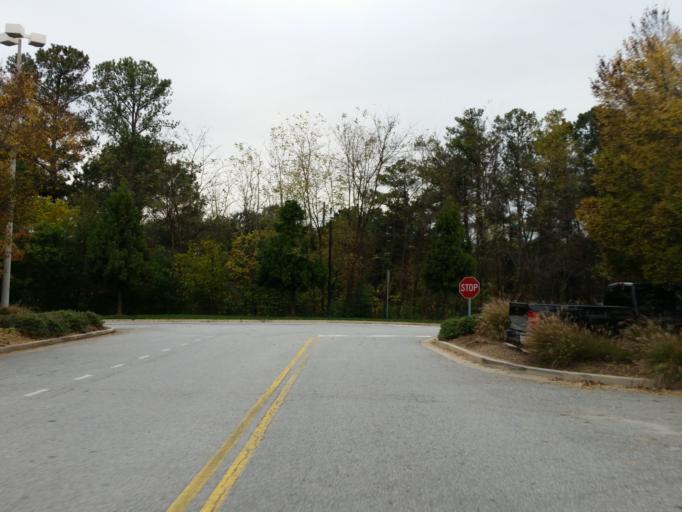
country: US
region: Georgia
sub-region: Cobb County
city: Vinings
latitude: 33.8799
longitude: -84.4720
